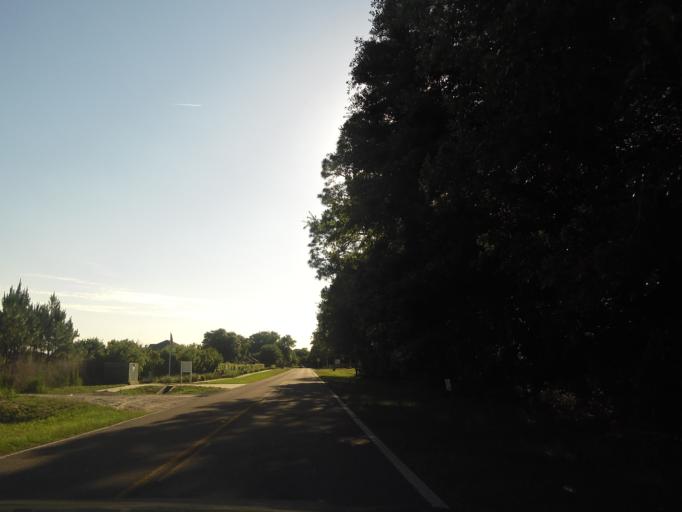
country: US
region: Florida
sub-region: Duval County
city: Atlantic Beach
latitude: 30.4592
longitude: -81.5277
